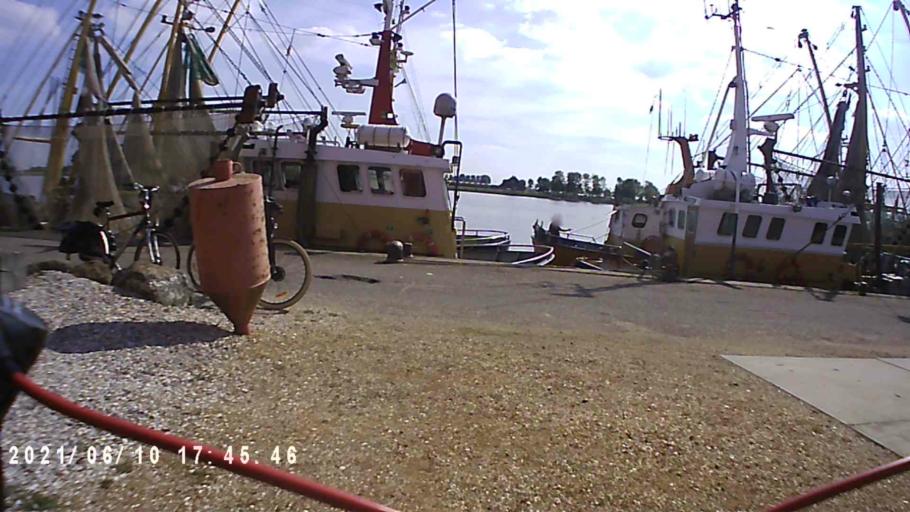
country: NL
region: Groningen
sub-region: Gemeente De Marne
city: Ulrum
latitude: 53.3354
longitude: 6.3026
